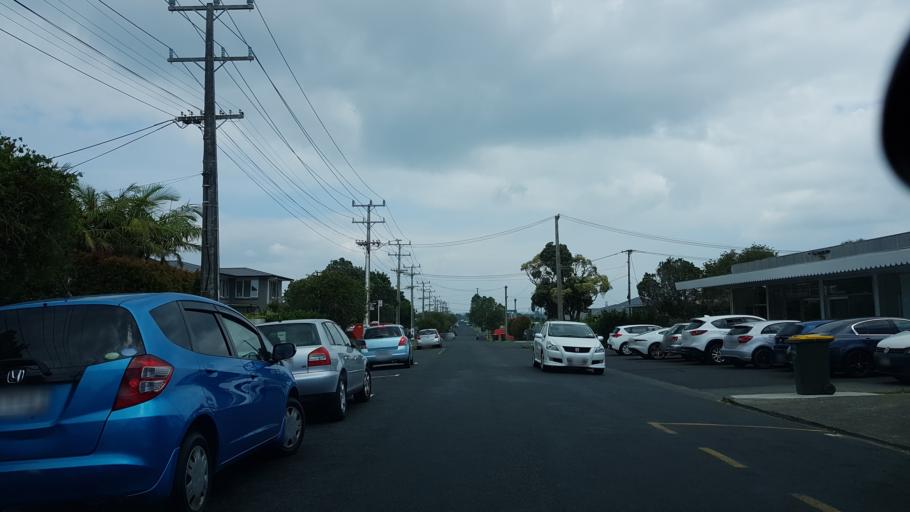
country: NZ
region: Auckland
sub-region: Auckland
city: North Shore
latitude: -36.8036
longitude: 174.7839
